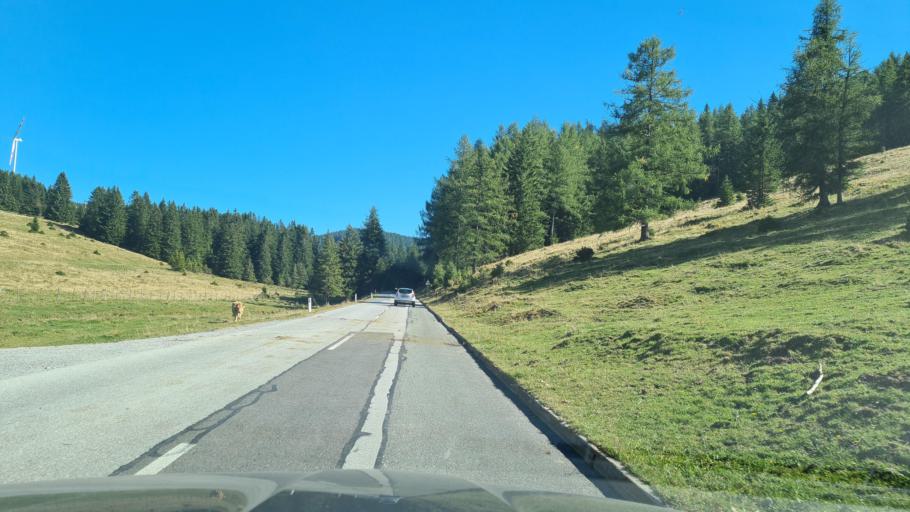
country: AT
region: Styria
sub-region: Politischer Bezirk Weiz
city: Gasen
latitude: 47.3497
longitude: 15.5306
